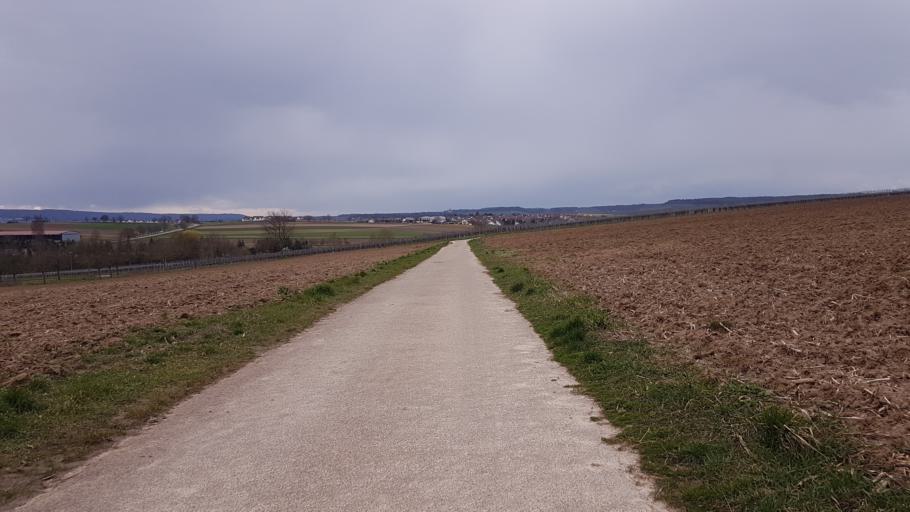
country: DE
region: Baden-Wuerttemberg
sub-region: Regierungsbezirk Stuttgart
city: Brackenheim
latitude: 49.0842
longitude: 9.0978
